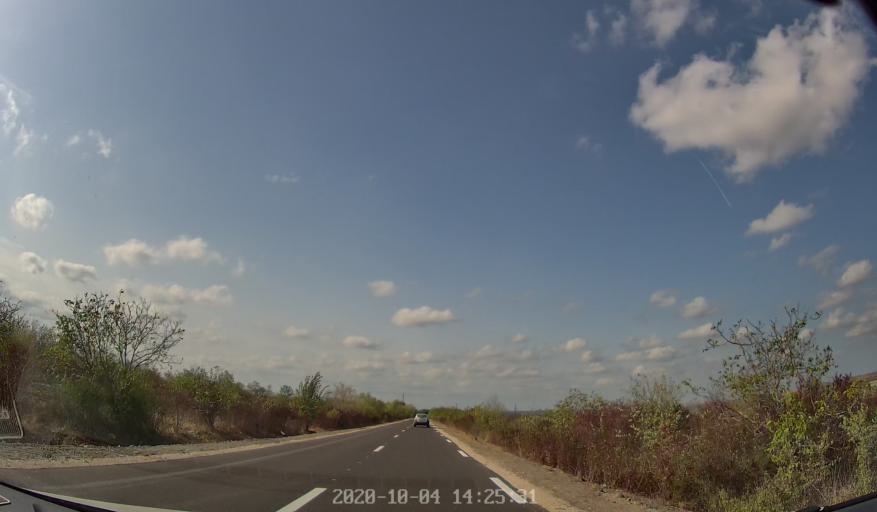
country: MD
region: Rezina
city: Saharna
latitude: 47.6209
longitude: 28.8977
